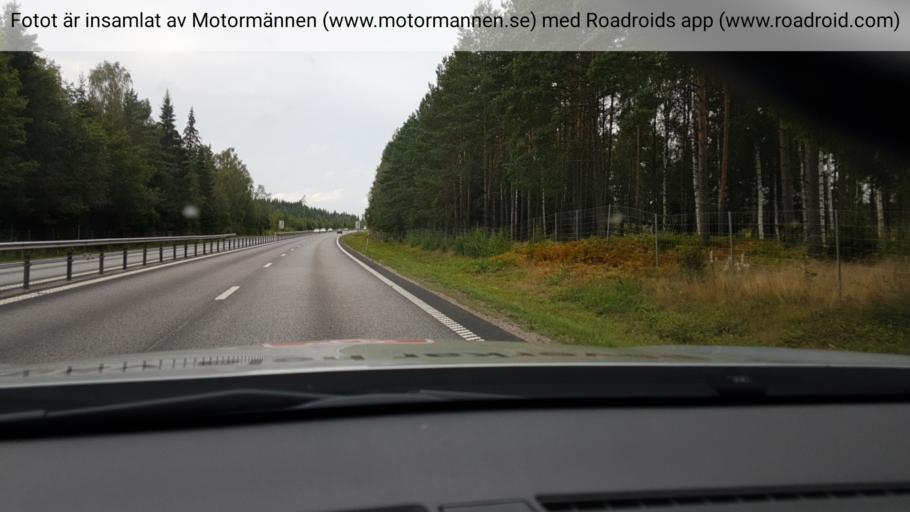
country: SE
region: Vaestra Goetaland
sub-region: Boras Kommun
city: Dalsjofors
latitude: 57.6297
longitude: 13.0890
